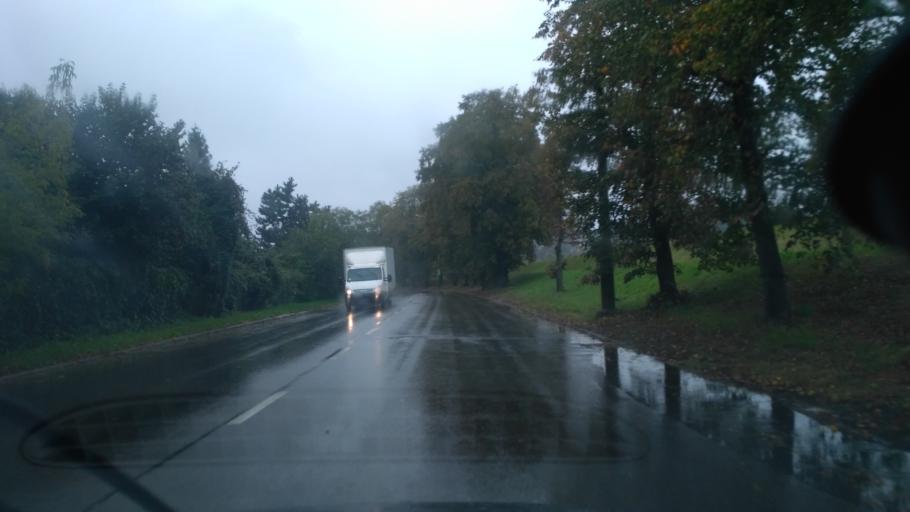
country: PL
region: Subcarpathian Voivodeship
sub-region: Powiat debicki
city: Debica
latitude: 50.0614
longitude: 21.3943
